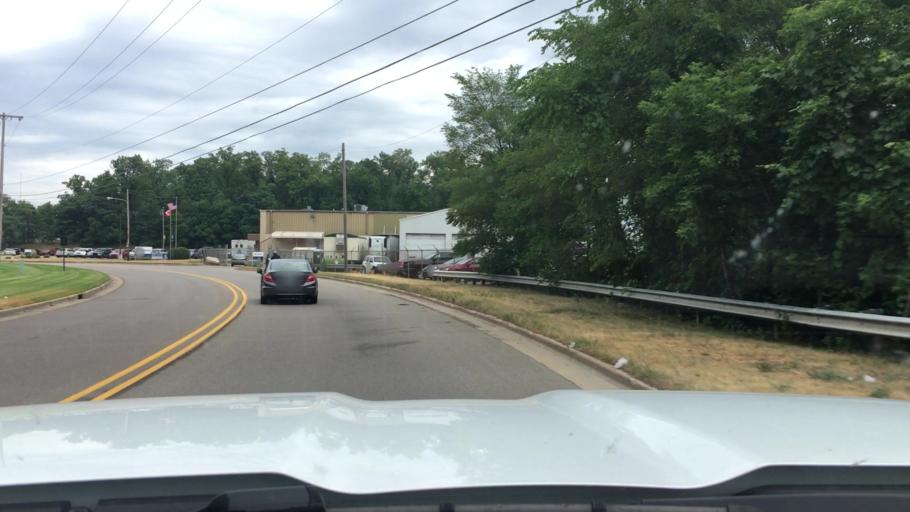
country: US
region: Michigan
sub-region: Kent County
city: Cutlerville
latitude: 42.8678
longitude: -85.6757
